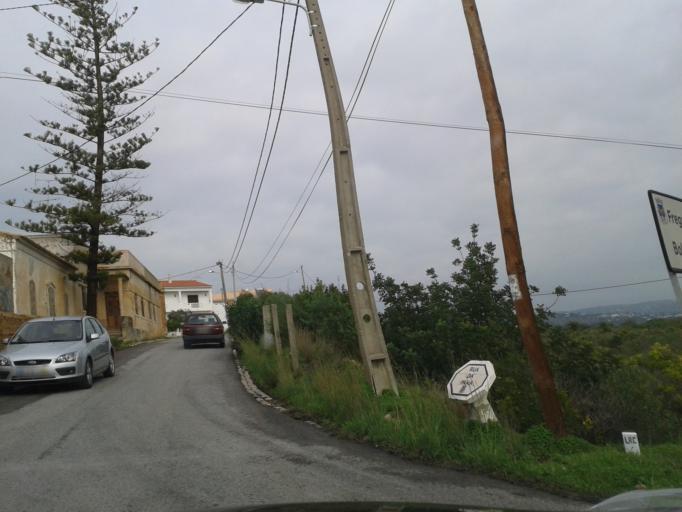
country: PT
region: Faro
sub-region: Loule
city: Boliqueime
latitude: 37.1100
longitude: -8.1868
